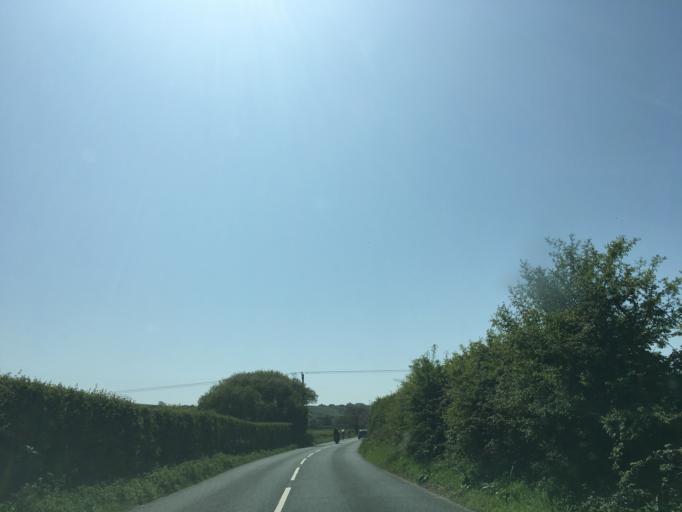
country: GB
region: England
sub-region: Isle of Wight
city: Niton
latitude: 50.5922
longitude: -1.2763
